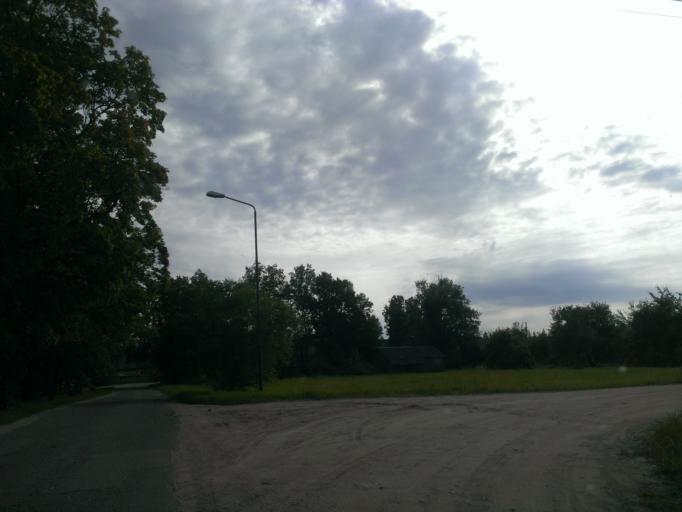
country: LV
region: Sigulda
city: Sigulda
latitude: 57.1686
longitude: 24.8265
